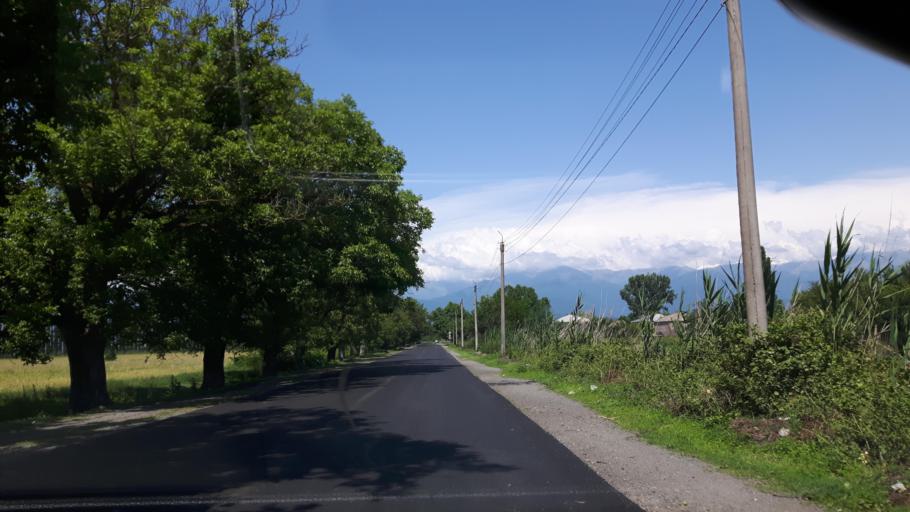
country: GE
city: Bagdadi
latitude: 41.7384
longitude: 46.1014
